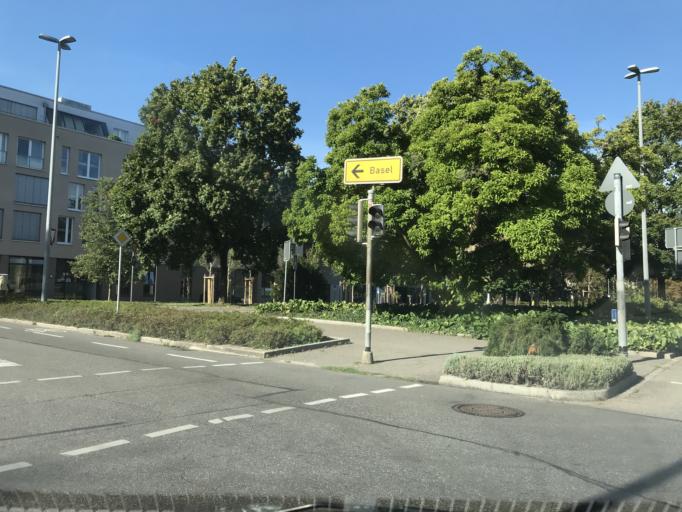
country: DE
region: Baden-Wuerttemberg
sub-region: Freiburg Region
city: Loerrach
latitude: 47.6090
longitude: 7.6600
